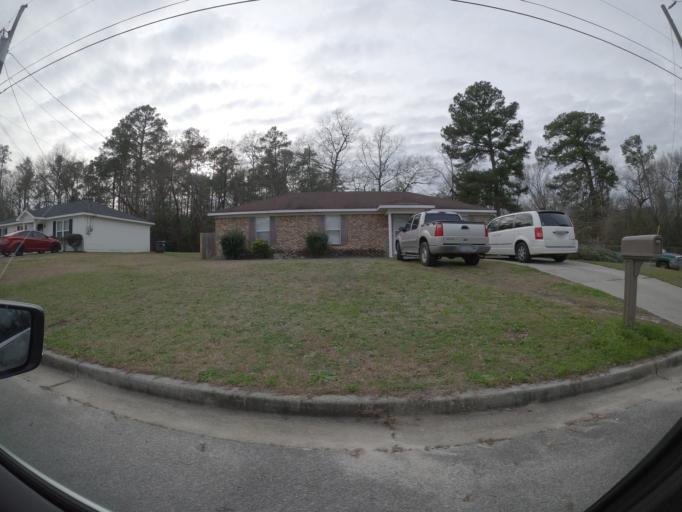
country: US
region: Georgia
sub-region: Columbia County
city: Grovetown
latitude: 33.4610
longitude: -82.1988
